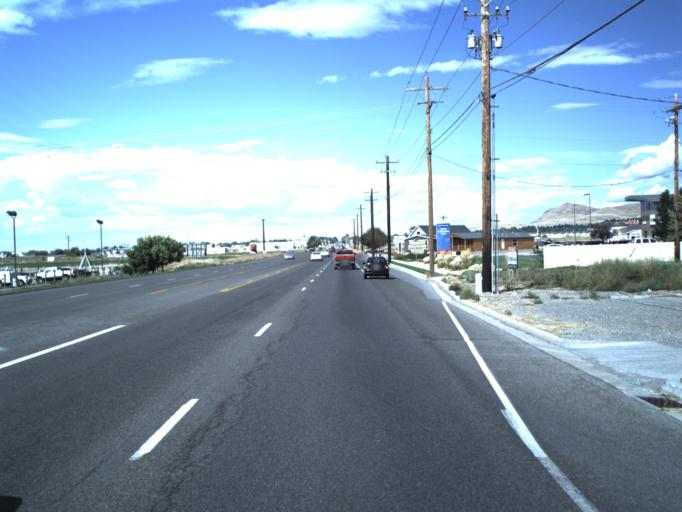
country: US
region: Utah
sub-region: Cache County
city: Hyde Park
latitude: 41.8053
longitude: -111.8333
